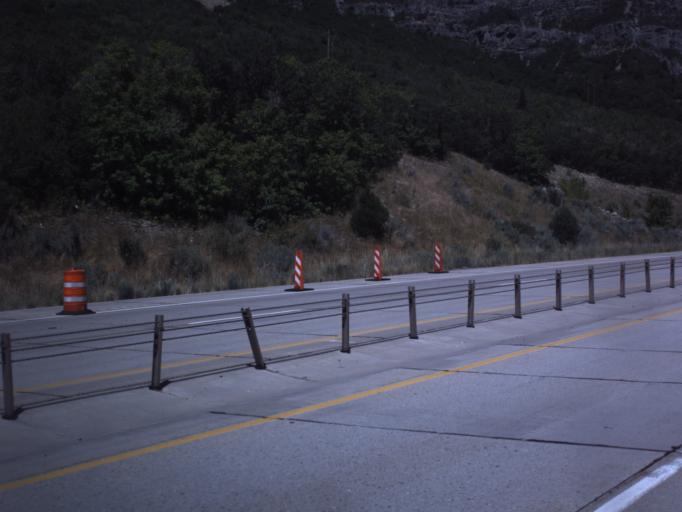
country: US
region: Utah
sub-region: Utah County
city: Orem
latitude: 40.3452
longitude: -111.5999
